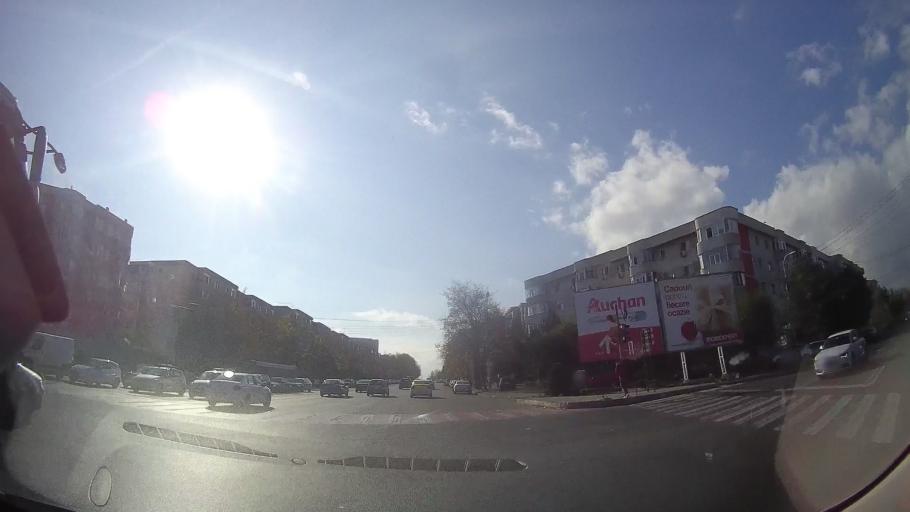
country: RO
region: Constanta
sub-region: Municipiul Constanta
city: Constanta
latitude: 44.1577
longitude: 28.6312
